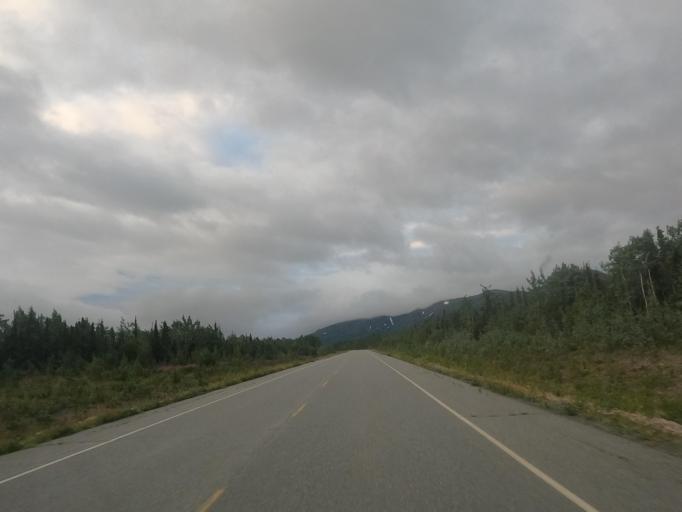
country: CA
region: Yukon
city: Haines Junction
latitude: 60.3135
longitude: -137.0421
